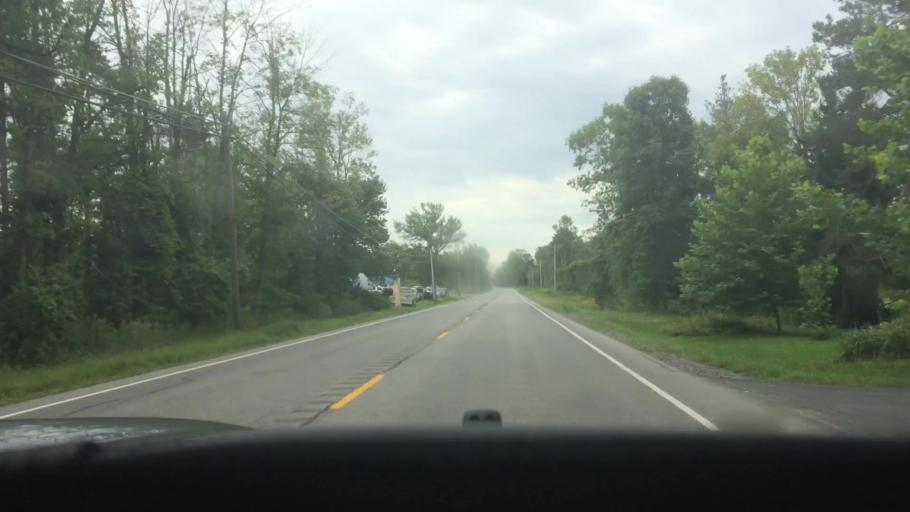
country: US
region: New York
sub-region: St. Lawrence County
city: Ogdensburg
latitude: 44.6506
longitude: -75.4432
